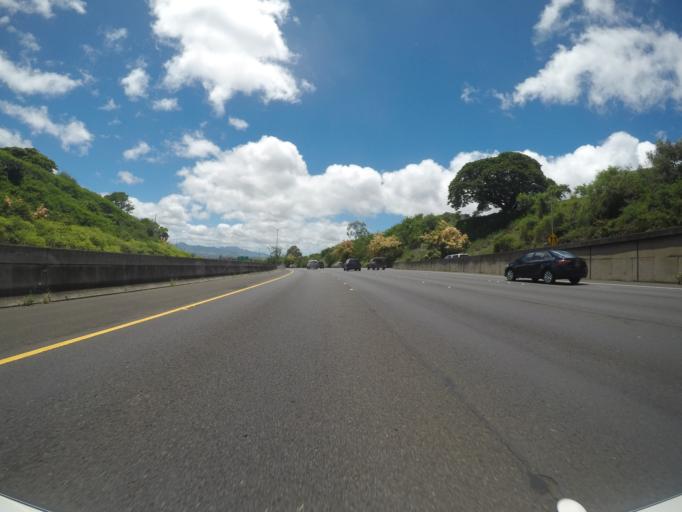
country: US
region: Hawaii
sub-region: Honolulu County
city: Halawa Heights
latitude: 21.3674
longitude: -157.9051
